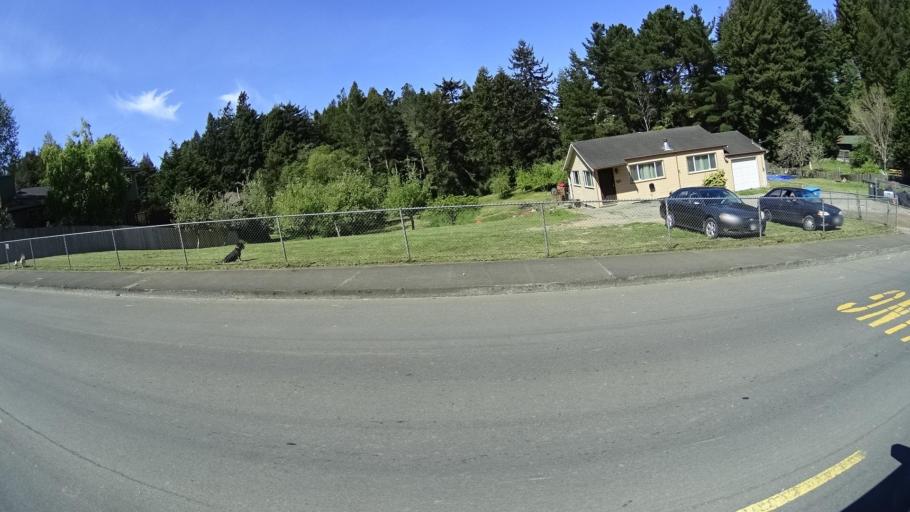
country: US
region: California
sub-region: Humboldt County
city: Myrtletown
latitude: 40.7896
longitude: -124.1489
